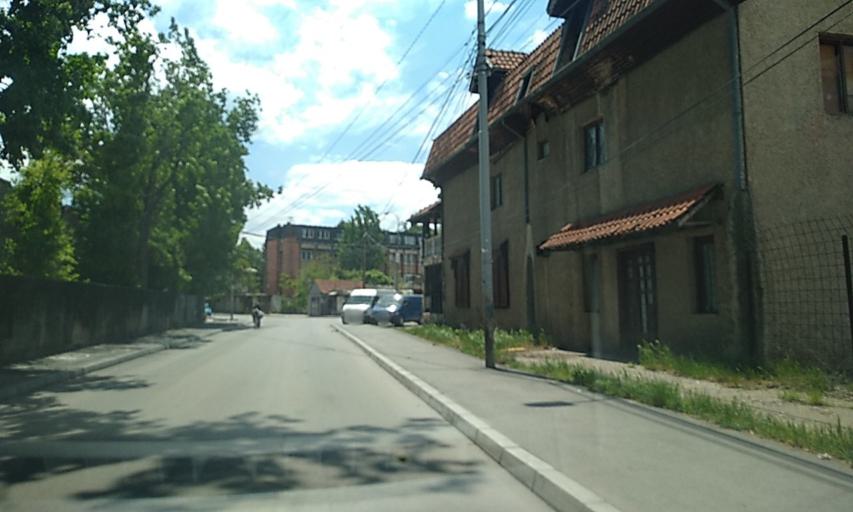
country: RS
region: Central Serbia
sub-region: Nisavski Okrug
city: Nis
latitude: 43.3206
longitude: 21.8826
